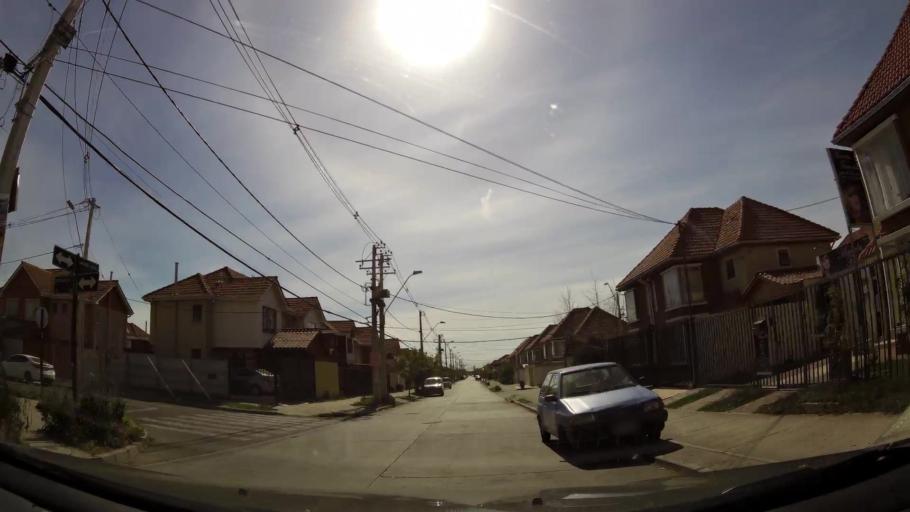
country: CL
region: Santiago Metropolitan
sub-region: Provincia de Cordillera
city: Puente Alto
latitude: -33.5933
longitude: -70.5448
